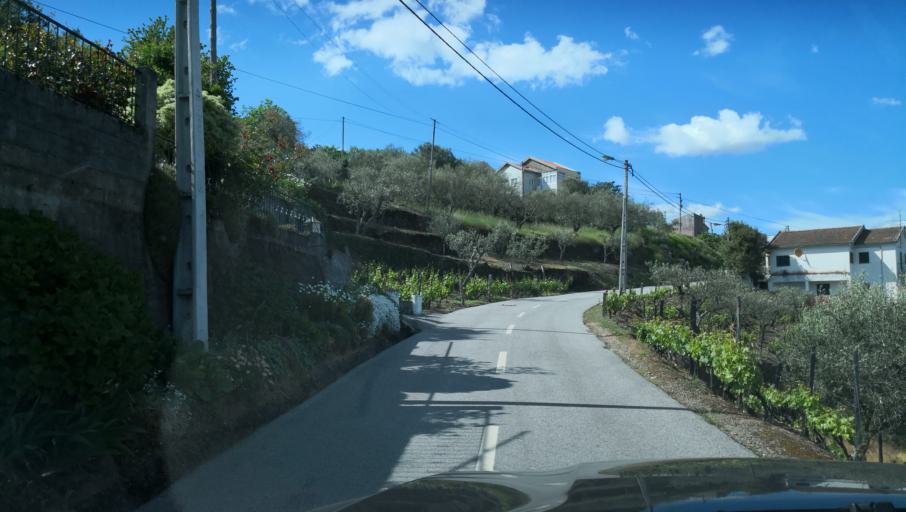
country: PT
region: Vila Real
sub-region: Vila Real
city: Vila Real
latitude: 41.2552
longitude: -7.7336
